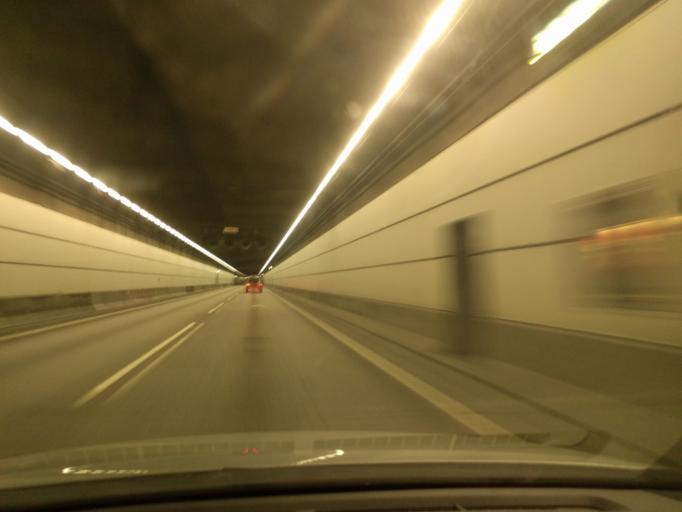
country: DK
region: Capital Region
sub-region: Tarnby Kommune
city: Tarnby
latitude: 55.6244
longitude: 12.6329
